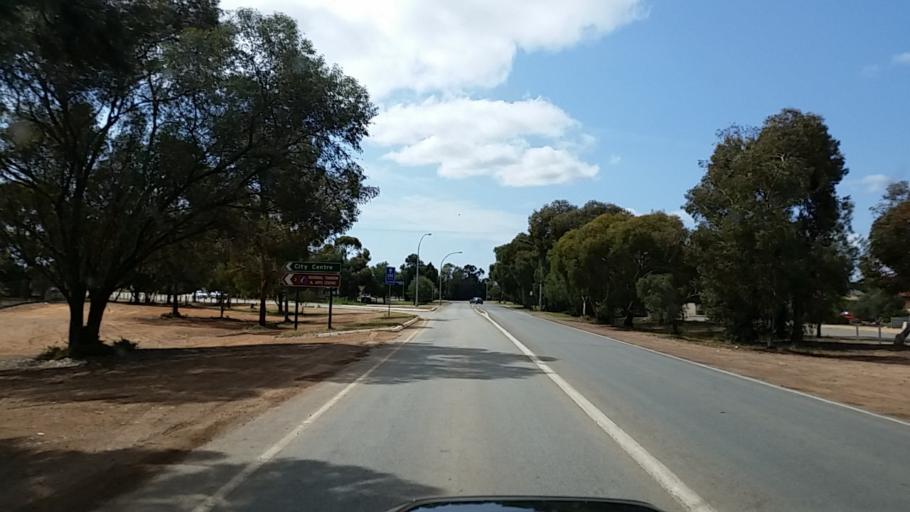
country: AU
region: South Australia
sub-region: Port Pirie City and Dists
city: Port Pirie
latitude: -33.2065
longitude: 138.0121
